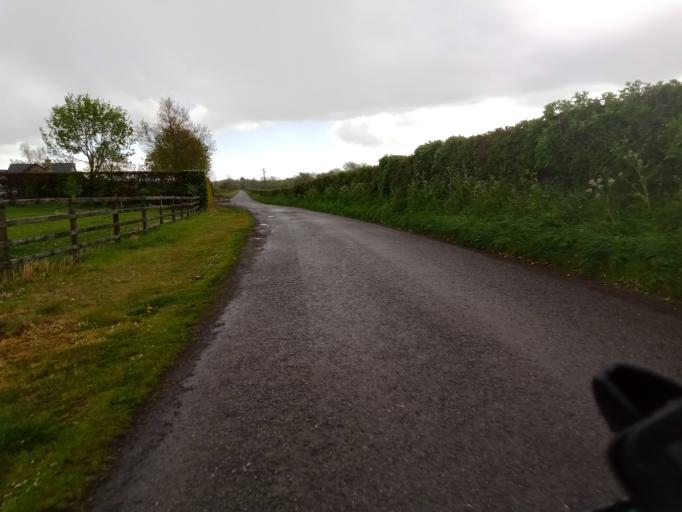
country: IE
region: Leinster
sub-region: Kilkenny
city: Kilkenny
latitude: 52.6813
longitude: -7.2676
